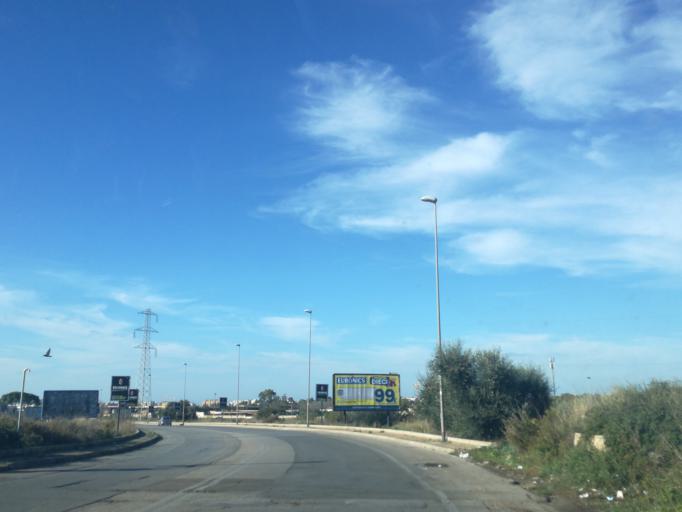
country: IT
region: Apulia
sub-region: Provincia di Bari
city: Bari
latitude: 41.1193
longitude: 16.8391
